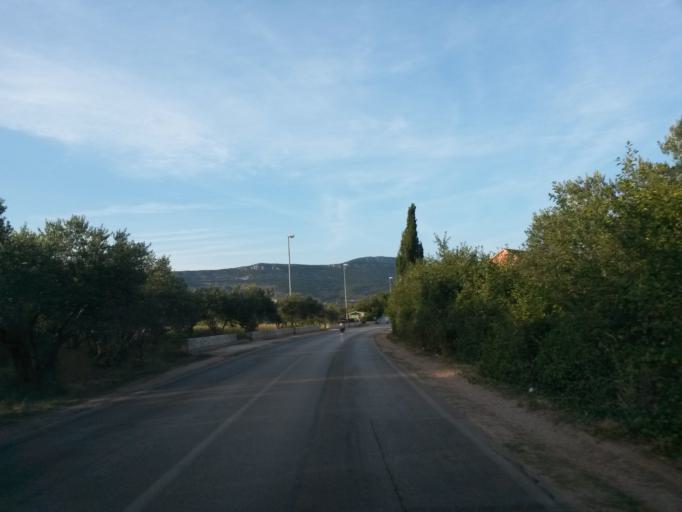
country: HR
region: Splitsko-Dalmatinska
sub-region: Grad Trogir
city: Trogir
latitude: 43.5438
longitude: 16.3127
